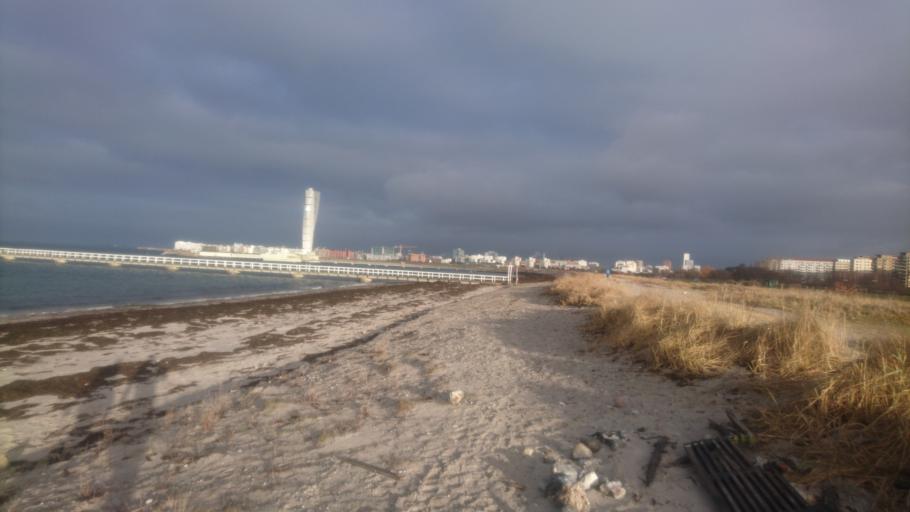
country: SE
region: Skane
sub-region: Malmo
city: Malmoe
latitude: 55.6017
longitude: 12.9619
